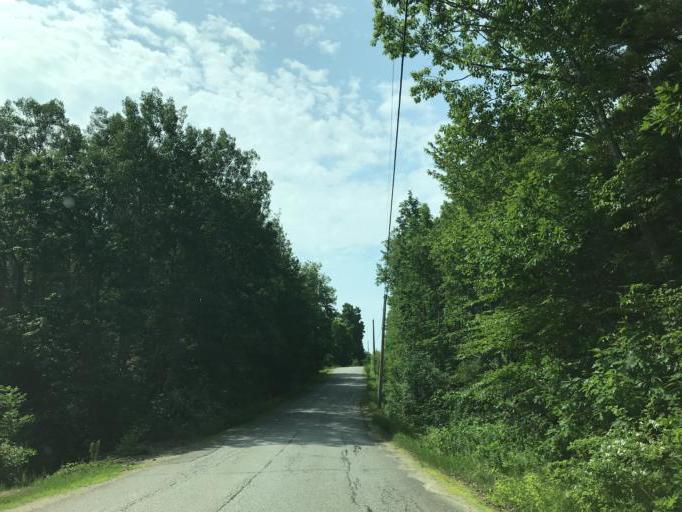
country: US
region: Maine
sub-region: Knox County
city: Hope
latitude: 44.2184
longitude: -69.1714
